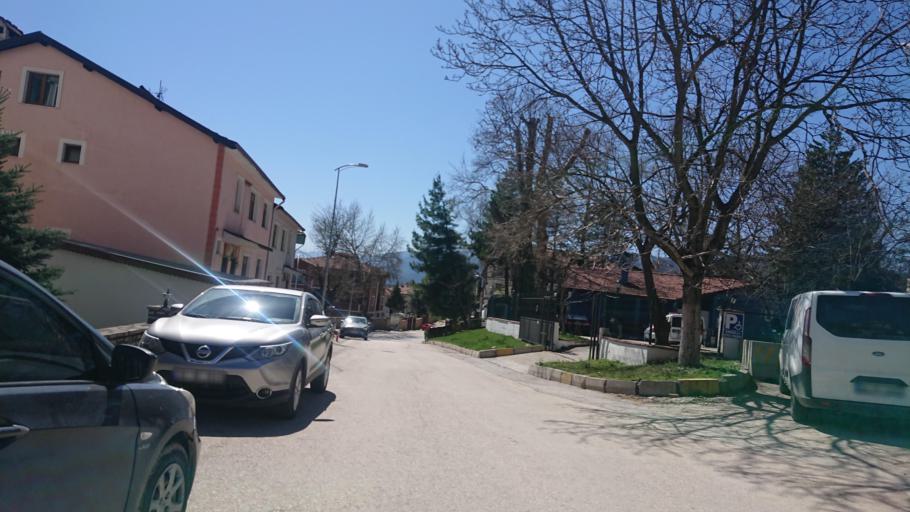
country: TR
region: Karabuk
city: Safranbolu
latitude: 41.2578
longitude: 32.6744
